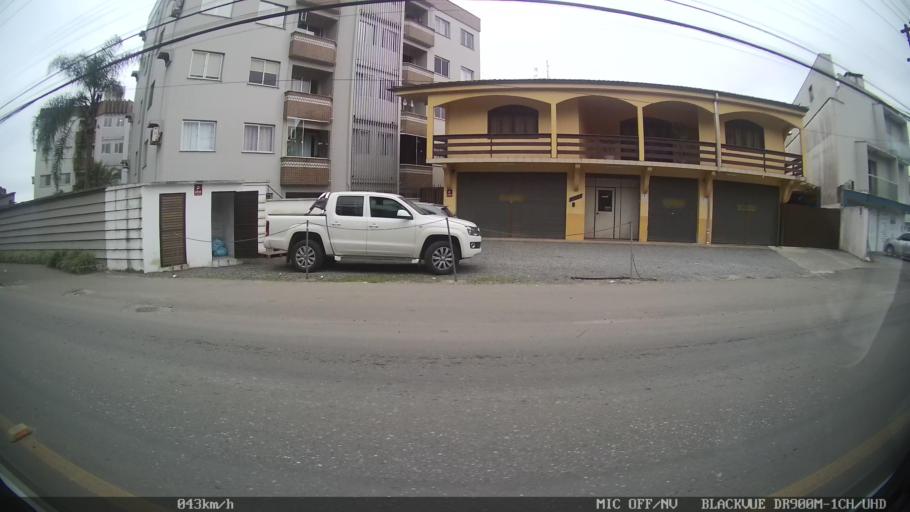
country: BR
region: Santa Catarina
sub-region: Joinville
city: Joinville
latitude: -26.2655
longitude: -48.8760
